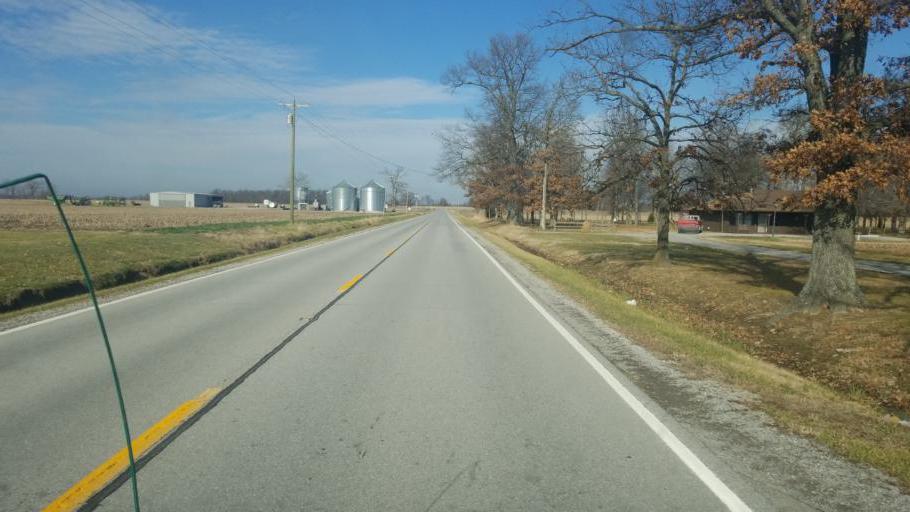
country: US
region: Illinois
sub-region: Saline County
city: Eldorado
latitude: 37.9002
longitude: -88.4530
